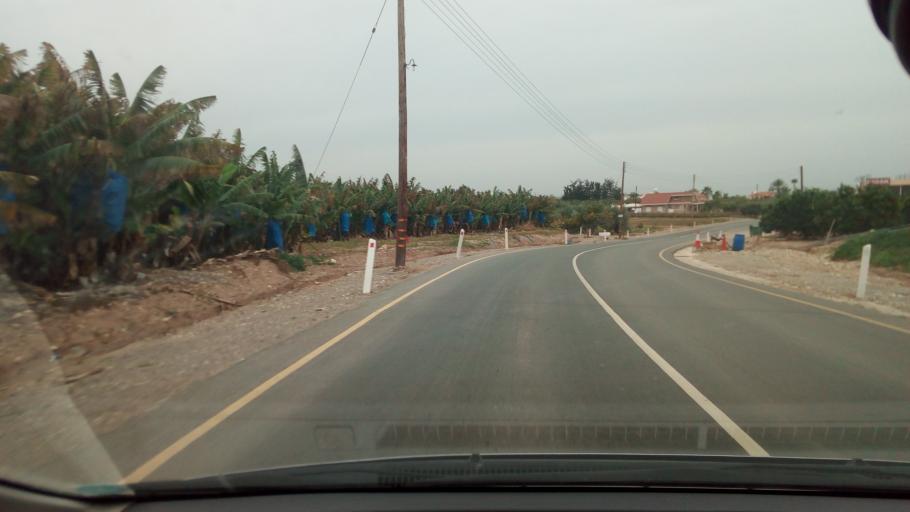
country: CY
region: Pafos
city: Pegeia
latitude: 34.8637
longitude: 32.3796
